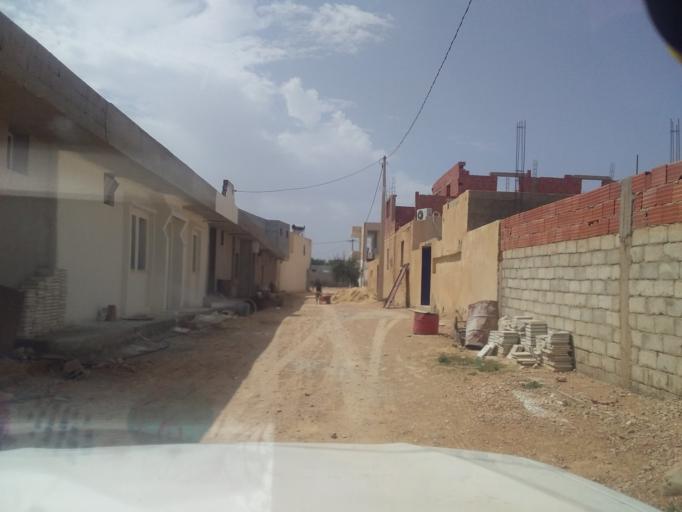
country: TN
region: Madanin
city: Medenine
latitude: 33.5880
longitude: 10.3252
